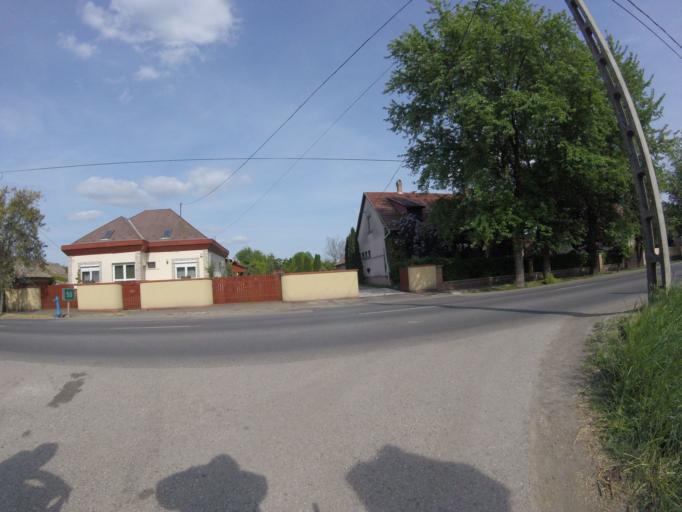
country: HU
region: Jasz-Nagykun-Szolnok
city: Jaszalsoszentgyorgy
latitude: 47.3746
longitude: 20.0895
